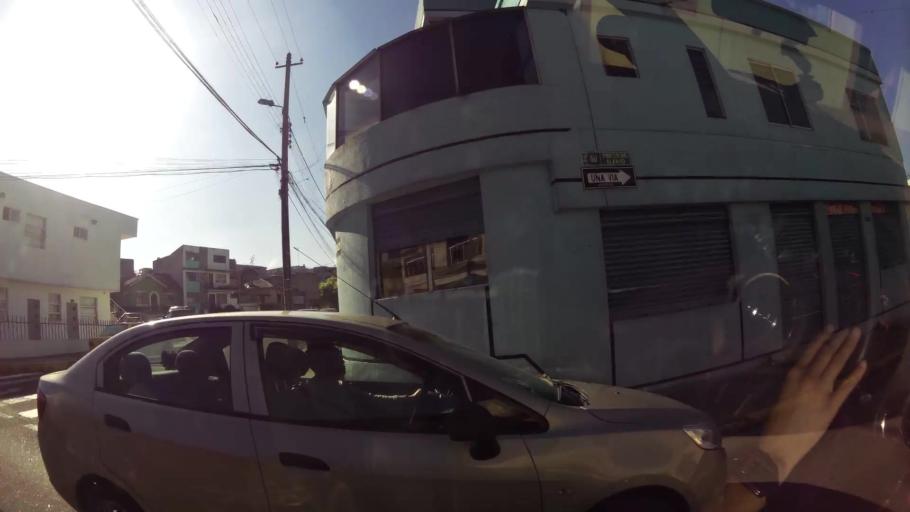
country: EC
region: Pichincha
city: Quito
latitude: -0.2437
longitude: -78.5222
